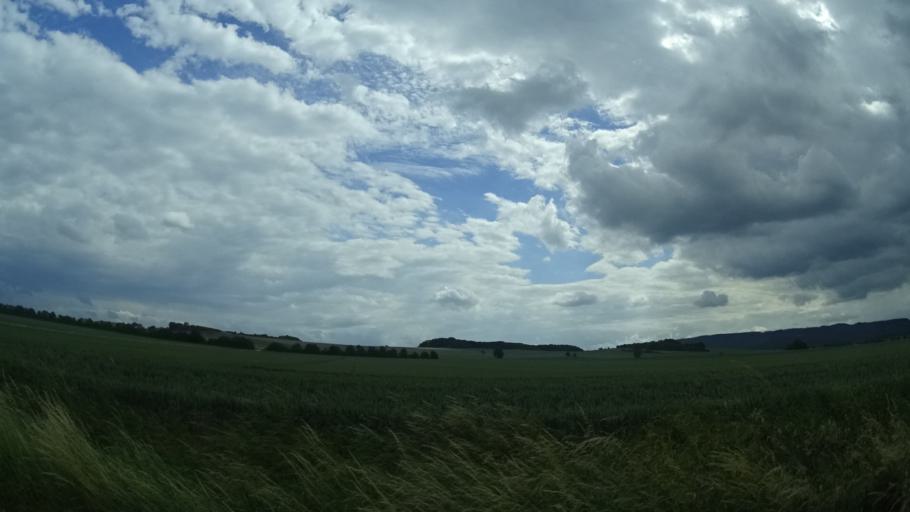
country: DE
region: Lower Saxony
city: Elze
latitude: 52.1597
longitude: 9.7164
